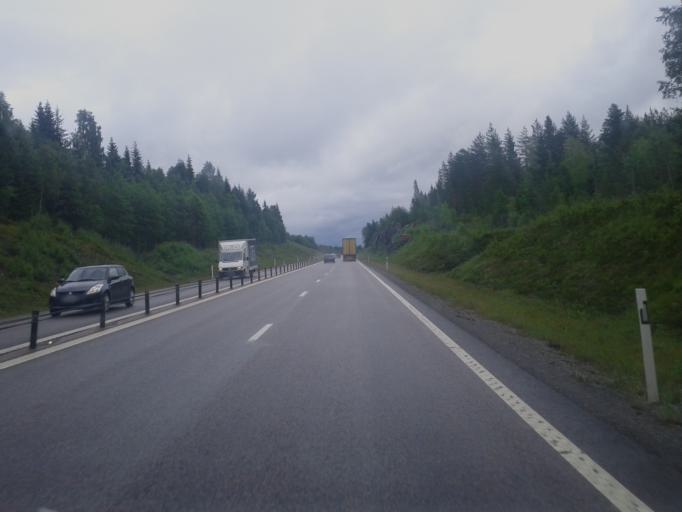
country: SE
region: Vaesternorrland
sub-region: Haernoesands Kommun
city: Haernoesand
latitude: 62.7102
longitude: 17.8865
